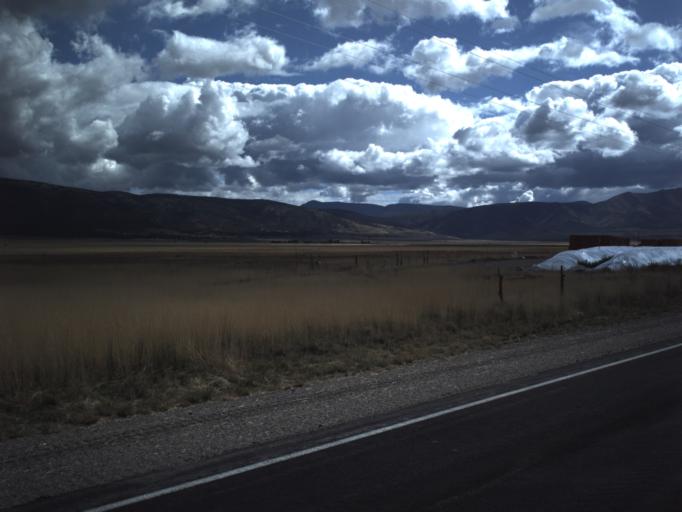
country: US
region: Utah
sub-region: Millard County
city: Fillmore
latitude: 38.8522
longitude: -112.4220
